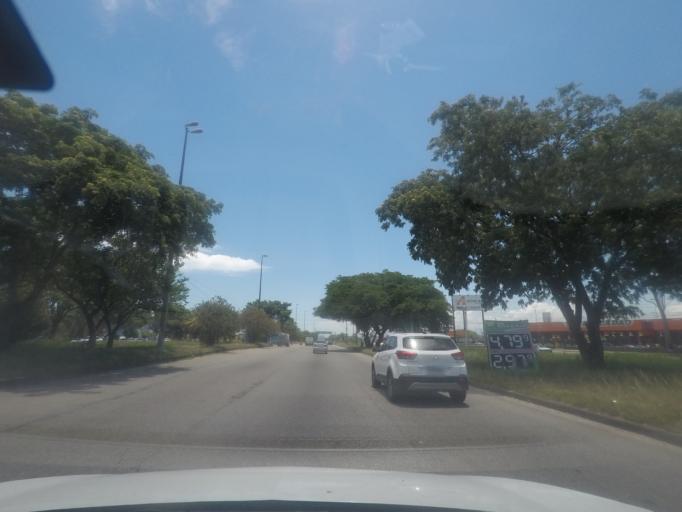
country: BR
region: Rio de Janeiro
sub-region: Itaguai
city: Itaguai
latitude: -22.8935
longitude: -43.6751
